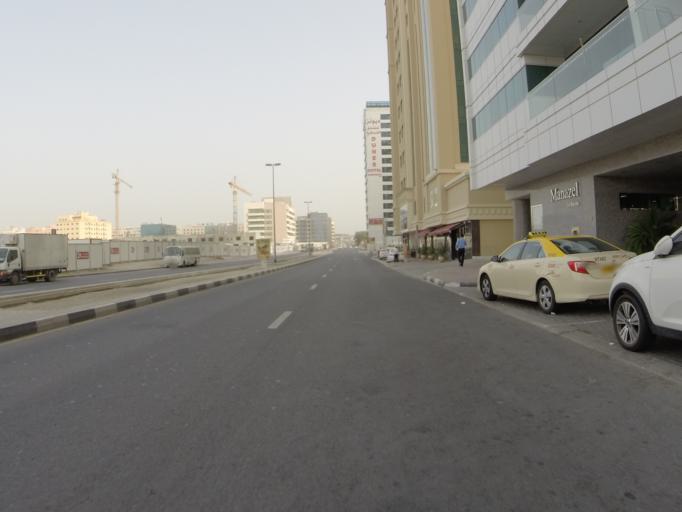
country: AE
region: Dubai
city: Dubai
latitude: 25.1133
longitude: 55.2004
